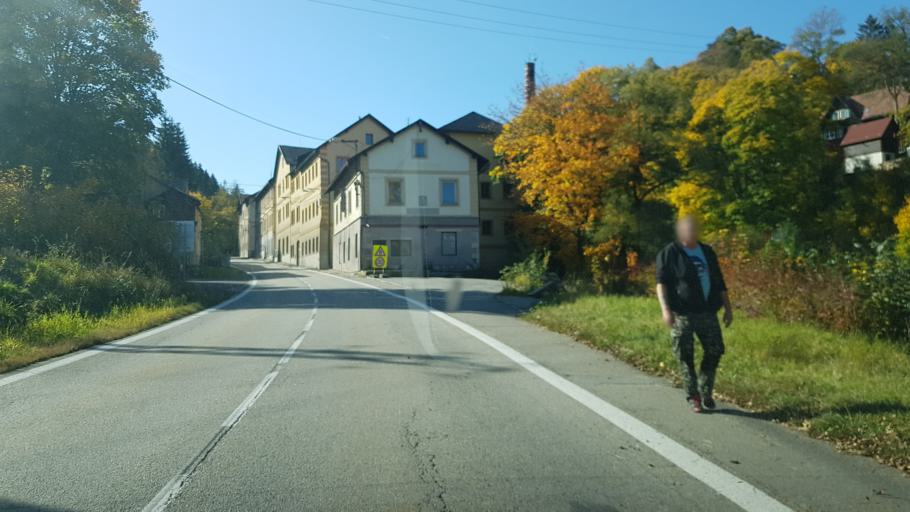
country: CZ
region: Jihocesky
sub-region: Okres Prachatice
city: Vimperk
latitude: 49.0510
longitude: 13.7717
